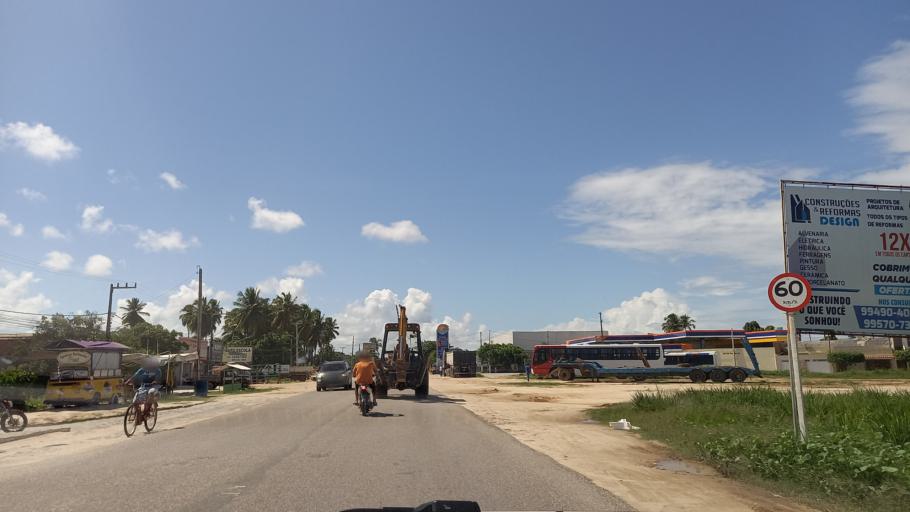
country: BR
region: Pernambuco
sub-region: Sao Jose Da Coroa Grande
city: Sao Jose da Coroa Grande
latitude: -8.8984
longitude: -35.1508
